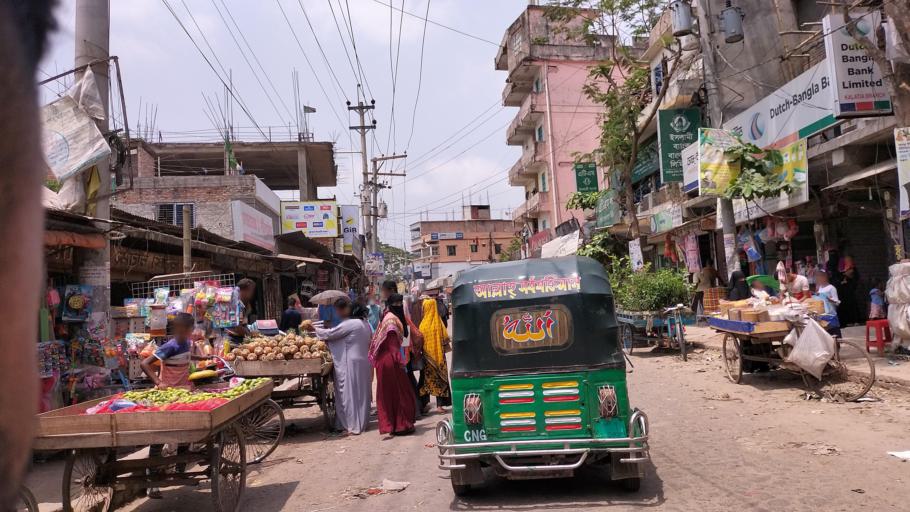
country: BD
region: Dhaka
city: Azimpur
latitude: 23.7313
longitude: 90.2747
